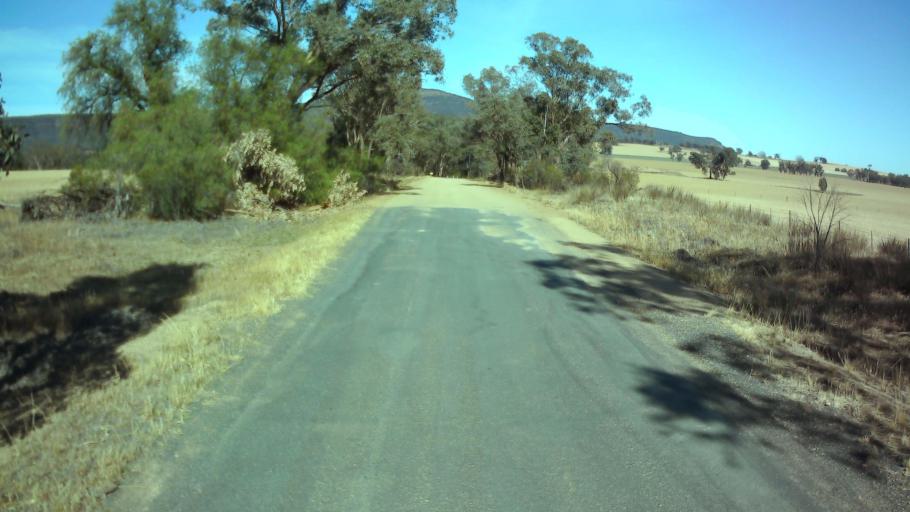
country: AU
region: New South Wales
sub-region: Weddin
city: Grenfell
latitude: -33.9033
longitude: 148.0443
